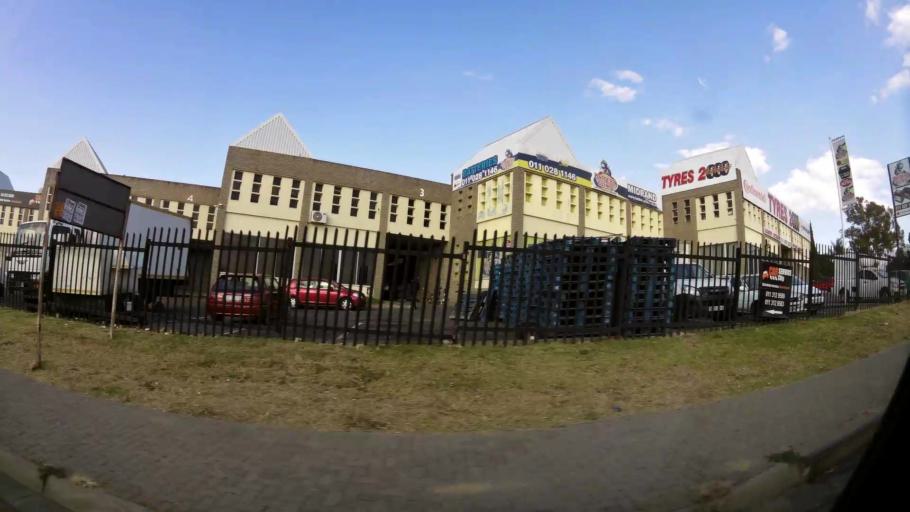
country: ZA
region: Gauteng
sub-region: City of Johannesburg Metropolitan Municipality
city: Midrand
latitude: -26.0084
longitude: 28.1218
